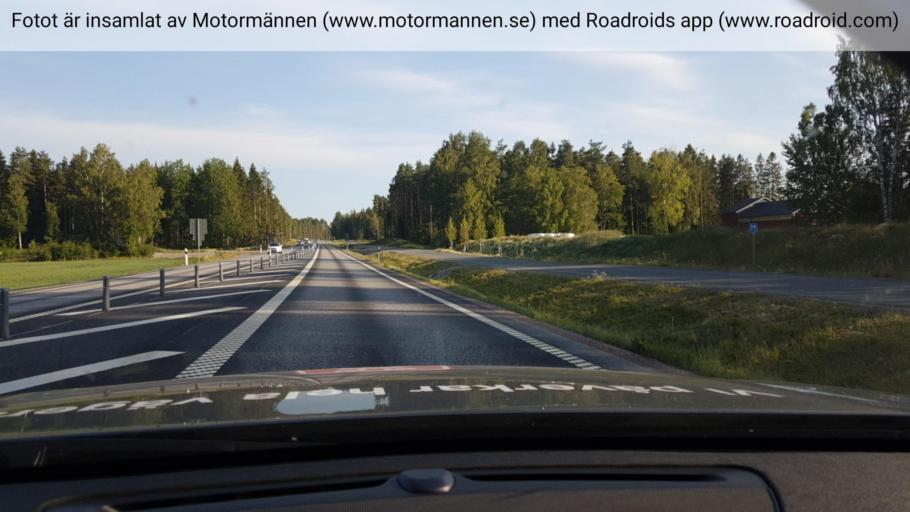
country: SE
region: Uppsala
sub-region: Osthammars Kommun
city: Gimo
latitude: 60.1054
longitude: 18.1253
